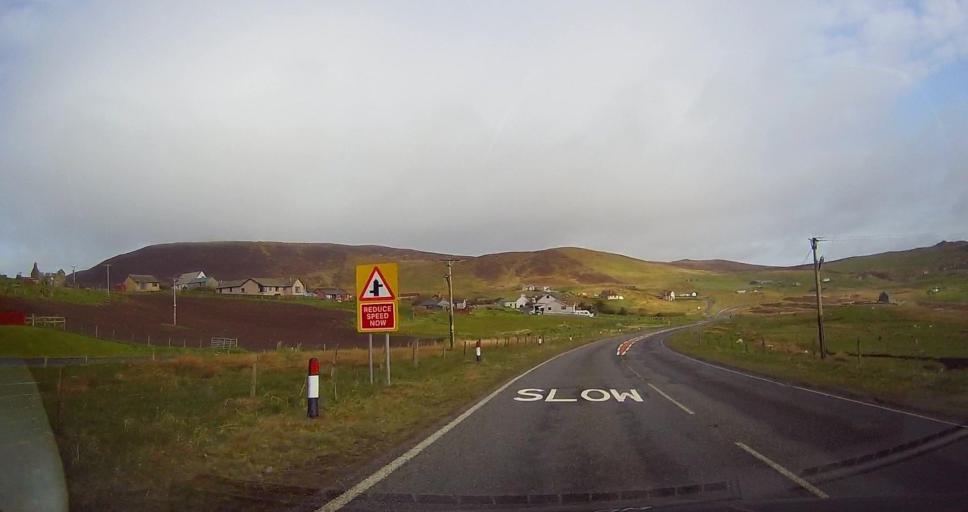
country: GB
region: Scotland
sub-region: Shetland Islands
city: Sandwick
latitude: 60.0960
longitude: -1.2331
